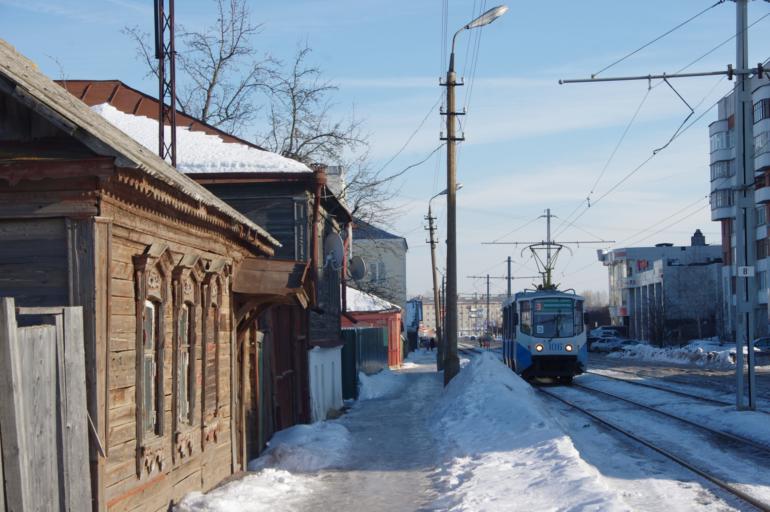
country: RU
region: Moskovskaya
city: Kolomna
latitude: 55.0971
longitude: 38.7600
